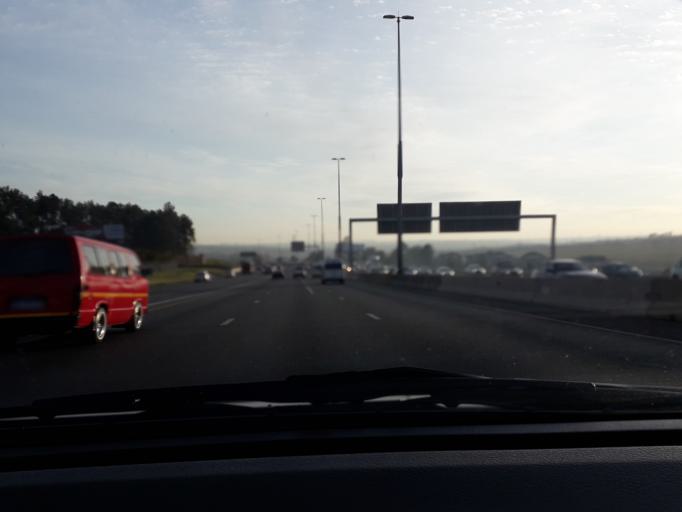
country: ZA
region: Gauteng
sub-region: City of Johannesburg Metropolitan Municipality
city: Midrand
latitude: -26.0432
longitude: 28.1012
